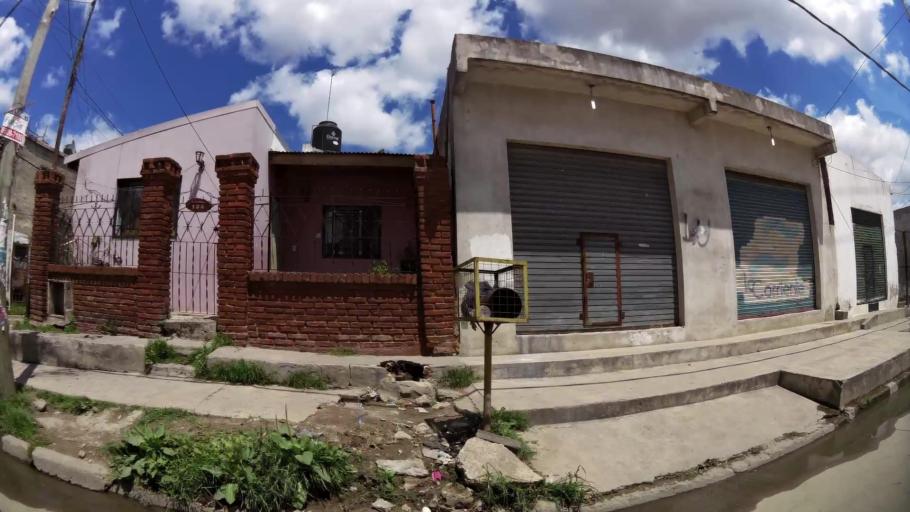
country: AR
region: Buenos Aires F.D.
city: Villa Lugano
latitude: -34.6960
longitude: -58.4415
